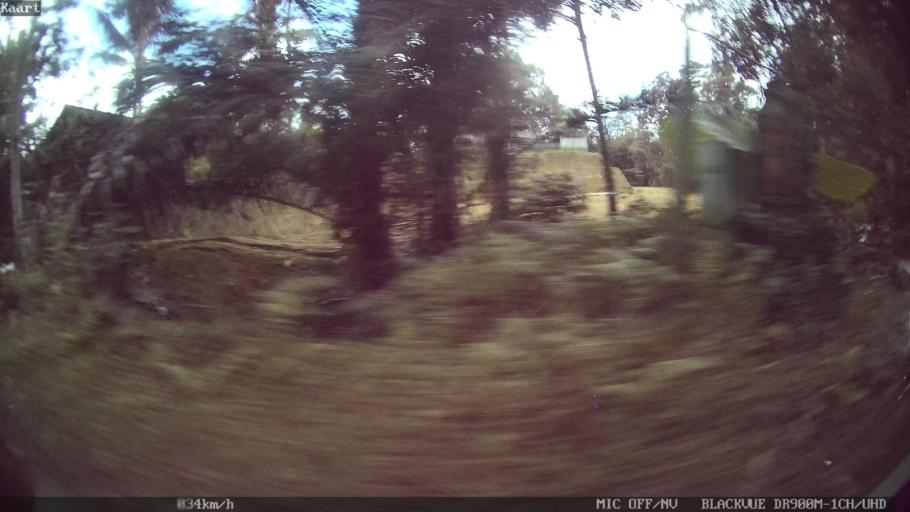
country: ID
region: Bali
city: Banjar Petak
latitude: -8.4393
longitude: 115.3206
